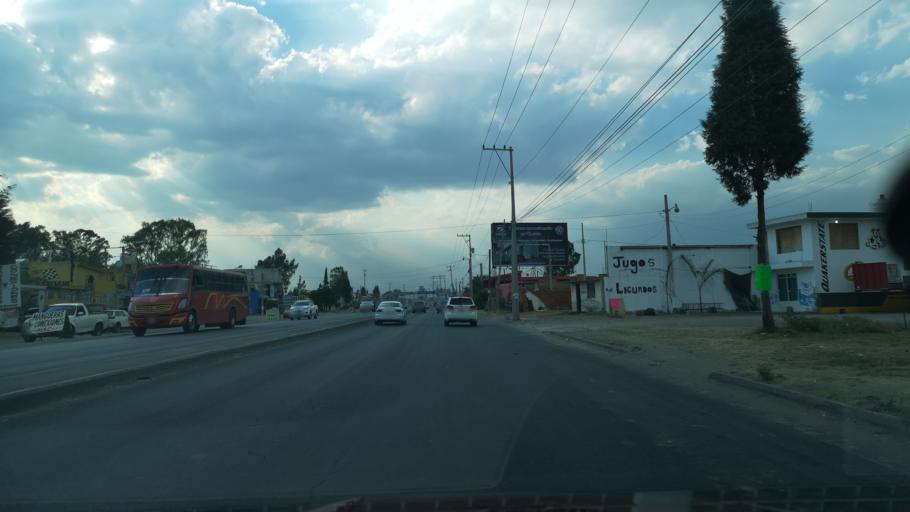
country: MX
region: Puebla
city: Cholula
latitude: 19.0751
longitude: -98.3200
